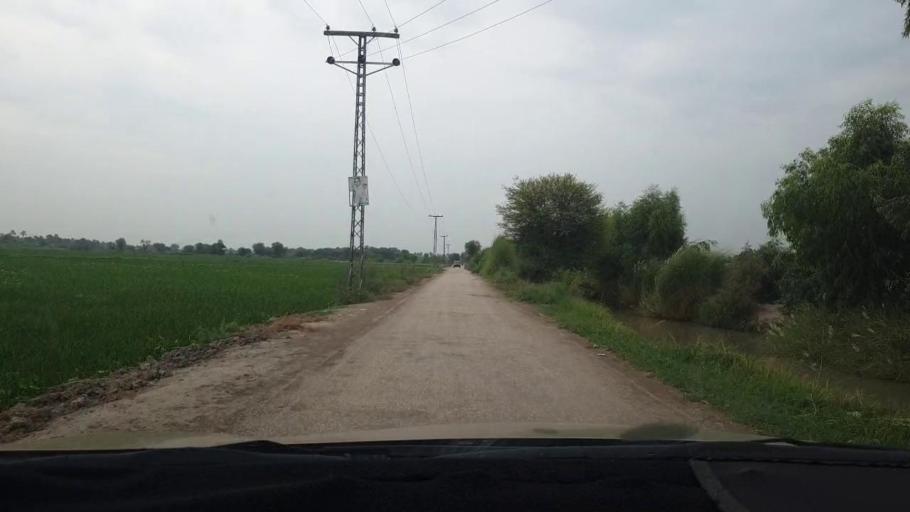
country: PK
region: Sindh
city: Larkana
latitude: 27.5797
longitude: 68.2354
